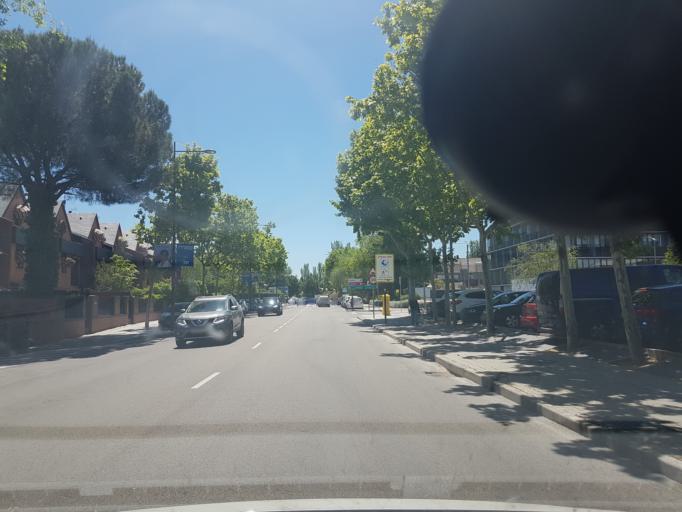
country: ES
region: Madrid
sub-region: Provincia de Madrid
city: Pozuelo de Alarcon
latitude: 40.4394
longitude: -3.8017
